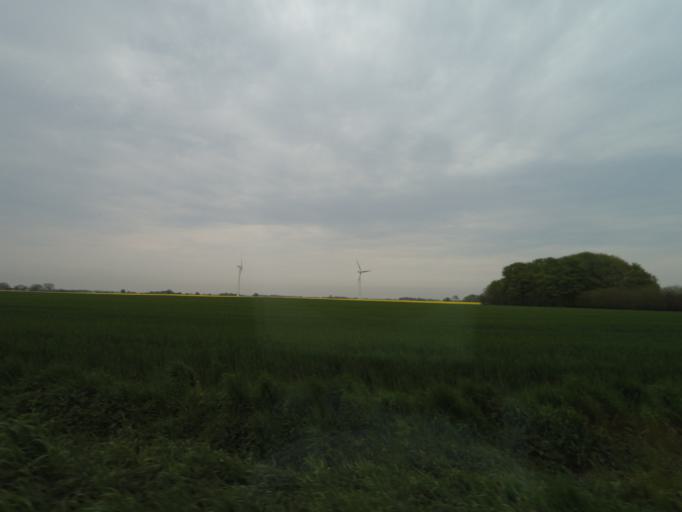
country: DK
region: South Denmark
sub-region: Faaborg-Midtfyn Kommune
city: Arslev
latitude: 55.3117
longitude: 10.4498
